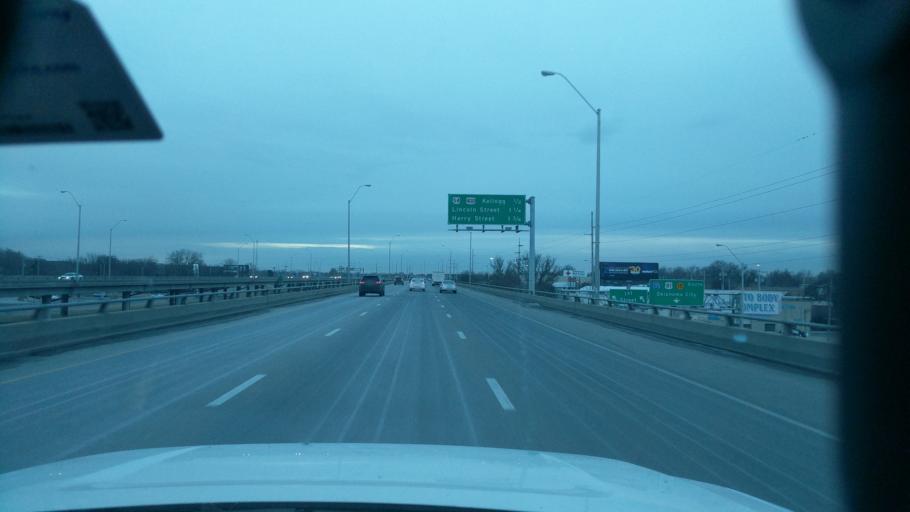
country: US
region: Kansas
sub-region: Sedgwick County
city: Wichita
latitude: 37.6900
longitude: -97.3146
